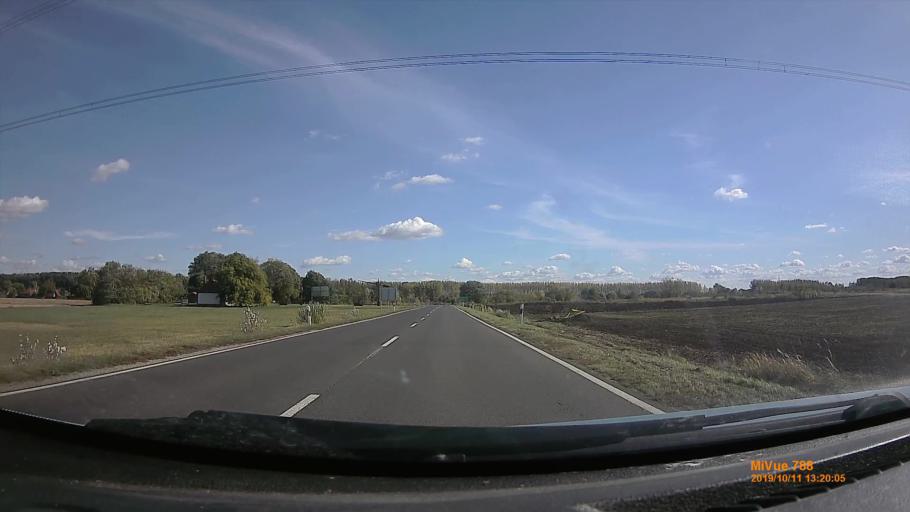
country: HU
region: Hajdu-Bihar
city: Balmazujvaros
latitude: 47.5539
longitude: 21.3202
